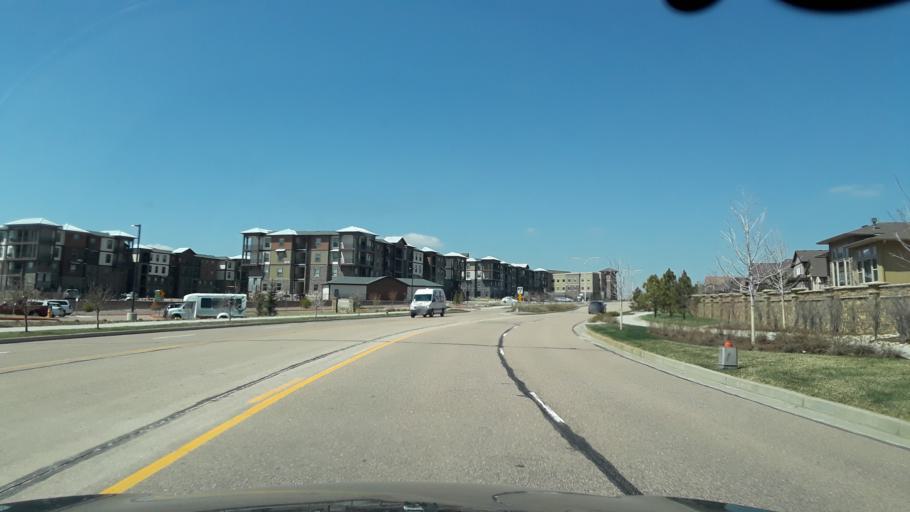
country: US
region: Colorado
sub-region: El Paso County
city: Black Forest
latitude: 38.9619
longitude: -104.7302
